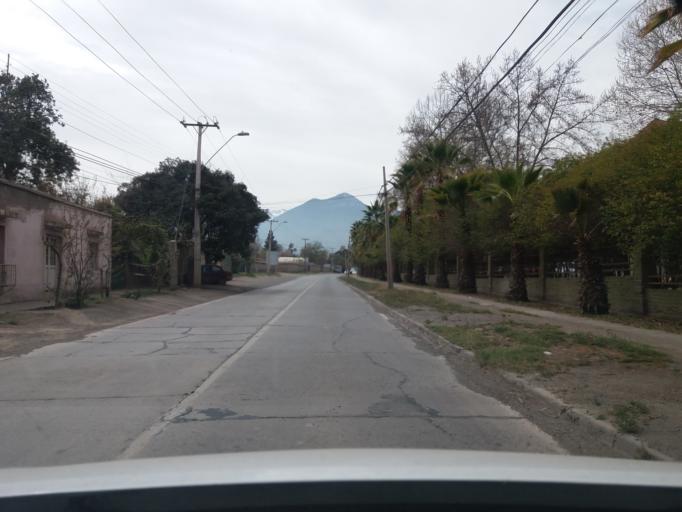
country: CL
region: Valparaiso
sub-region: Provincia de Los Andes
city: Los Andes
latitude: -32.8369
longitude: -70.5782
